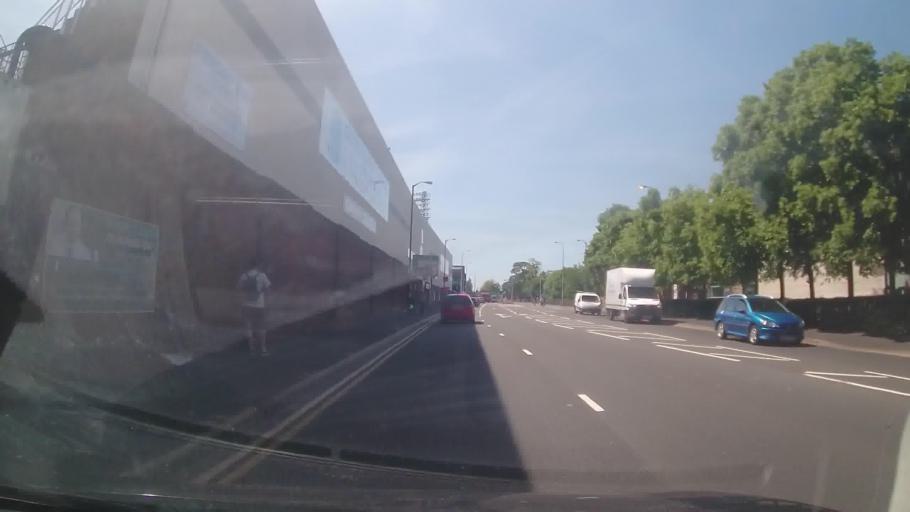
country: GB
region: England
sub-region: Herefordshire
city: Hereford
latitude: 52.0616
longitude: -2.7180
